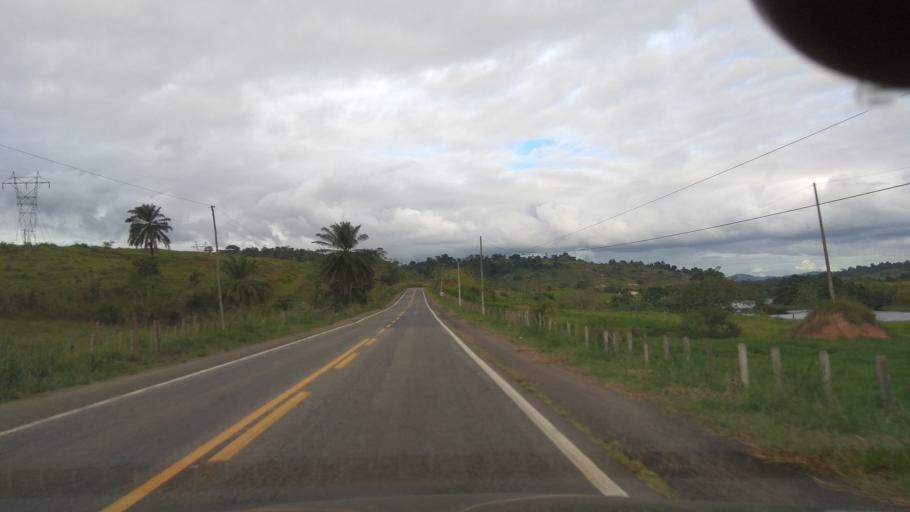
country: BR
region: Bahia
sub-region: Ipiau
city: Ipiau
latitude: -14.1775
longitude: -39.6708
